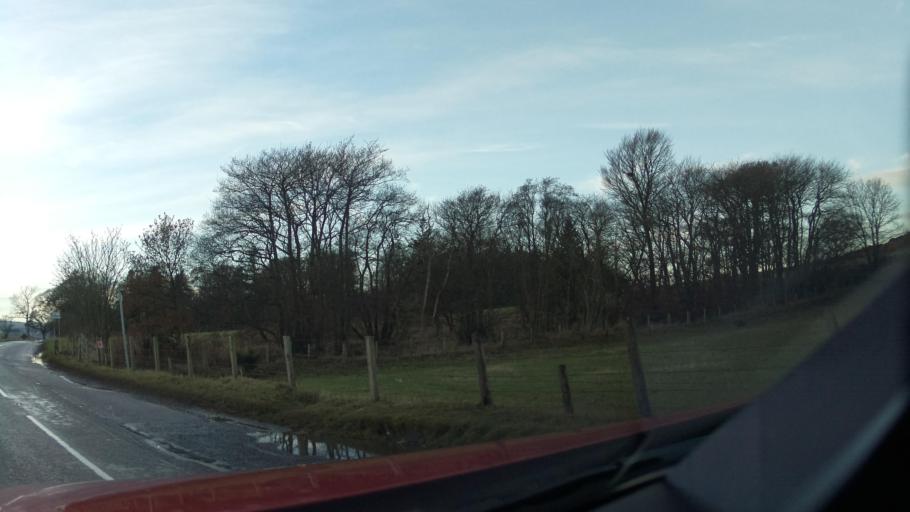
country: GB
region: Scotland
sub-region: Angus
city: Letham
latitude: 56.5795
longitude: -2.8062
